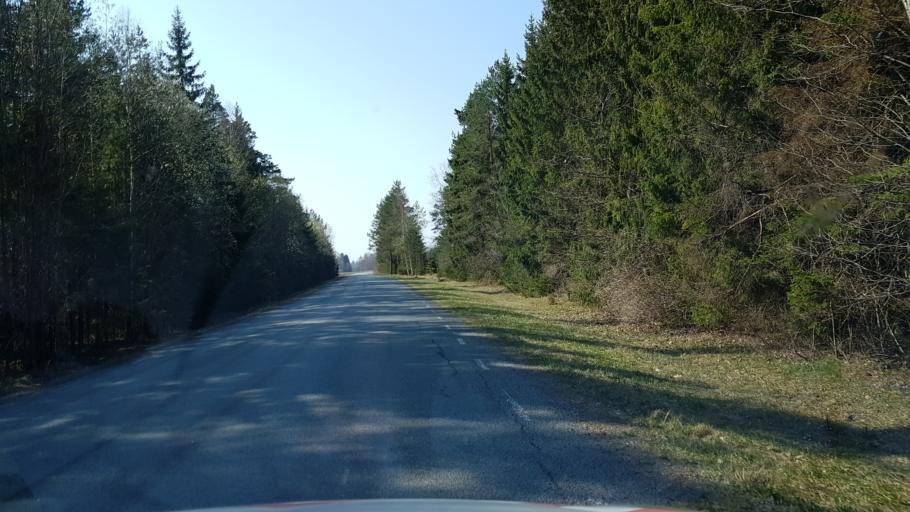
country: EE
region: Raplamaa
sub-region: Maerjamaa vald
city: Marjamaa
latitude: 58.8867
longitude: 24.3911
